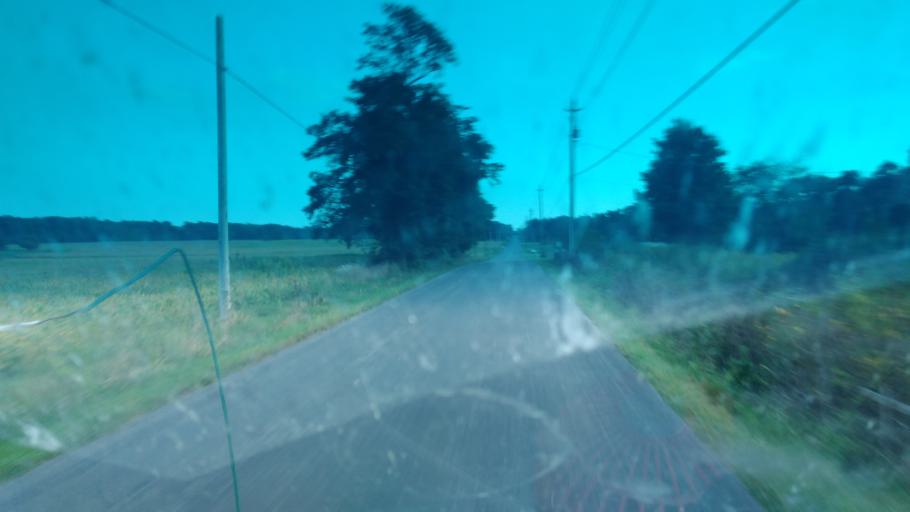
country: US
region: Ohio
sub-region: Crawford County
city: Galion
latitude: 40.7819
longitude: -82.8195
